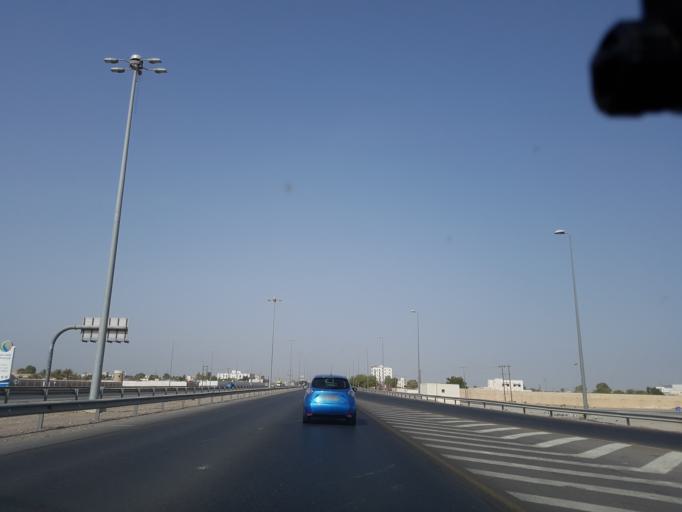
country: OM
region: Al Batinah
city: Barka'
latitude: 23.6847
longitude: 58.0190
